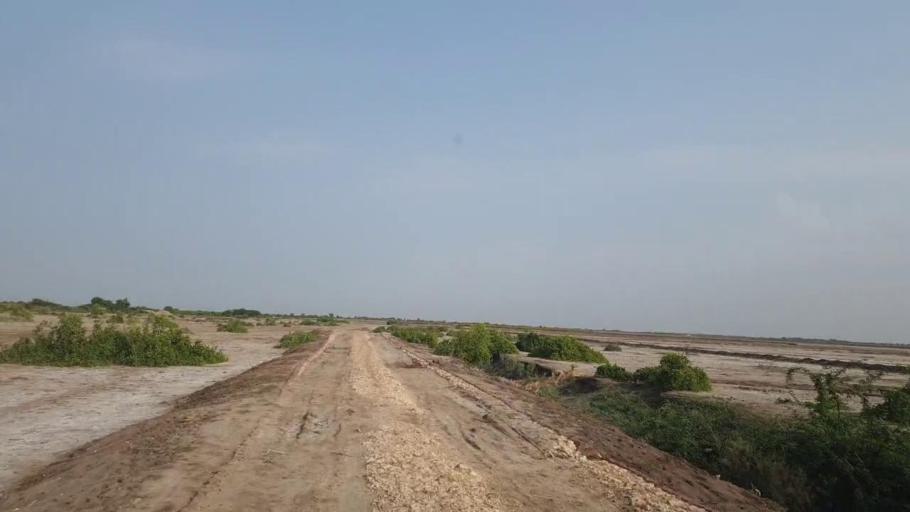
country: PK
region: Sindh
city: Kadhan
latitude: 24.4442
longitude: 68.8132
